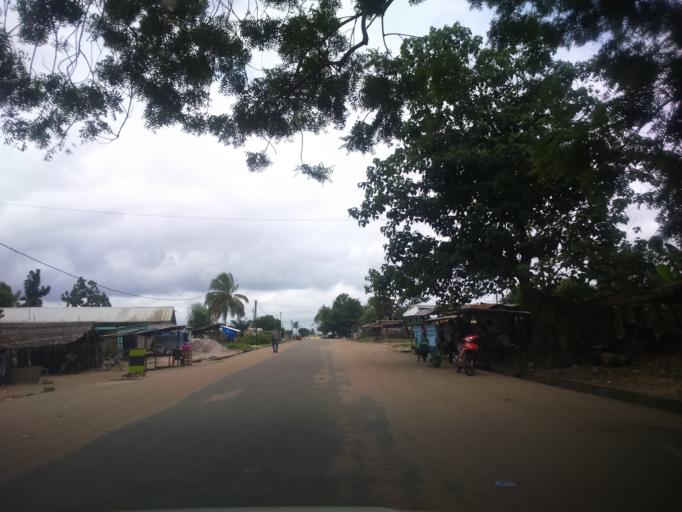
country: CI
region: Sud-Comoe
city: Adiake
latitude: 5.2887
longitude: -3.3041
